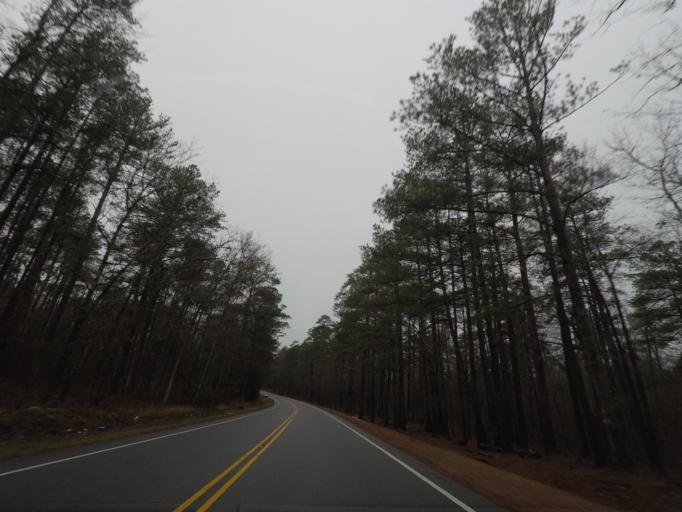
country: US
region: North Carolina
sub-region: Cumberland County
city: Spring Lake
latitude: 35.2534
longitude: -79.0008
